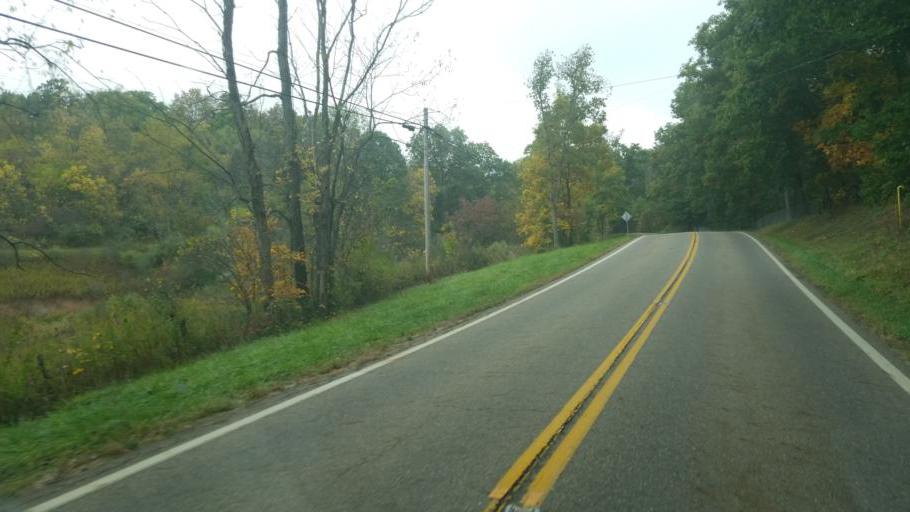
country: US
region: Ohio
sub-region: Carroll County
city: Lake Mohawk
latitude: 40.5928
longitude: -81.2634
